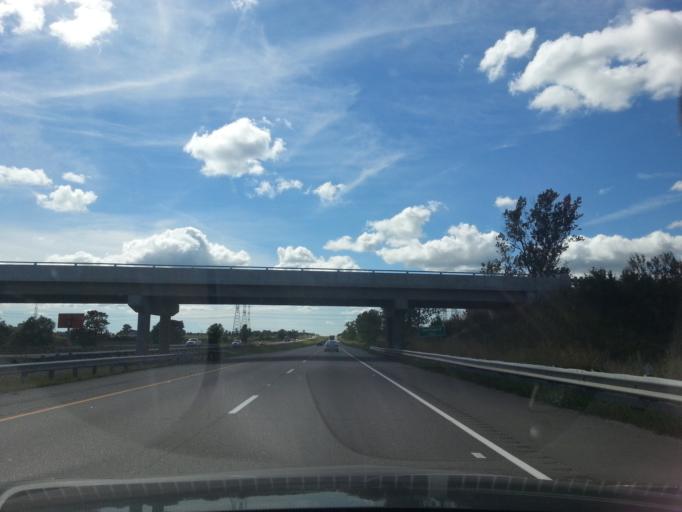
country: CA
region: Ontario
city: Napanee Downtown
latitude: 44.2526
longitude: -77.0050
